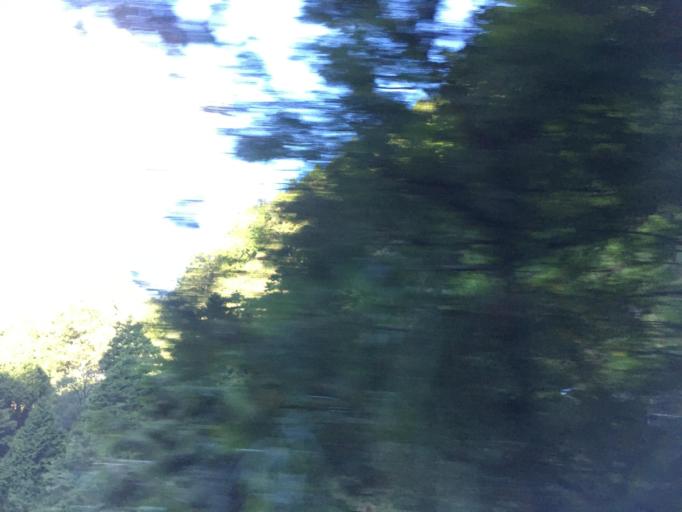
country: TW
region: Taiwan
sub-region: Yilan
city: Yilan
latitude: 24.5043
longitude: 121.5594
